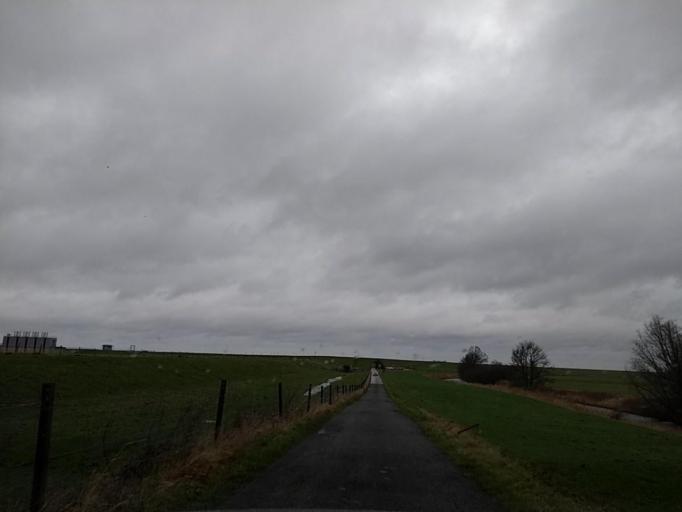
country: DE
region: Lower Saxony
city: Bunde
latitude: 53.2291
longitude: 7.2125
